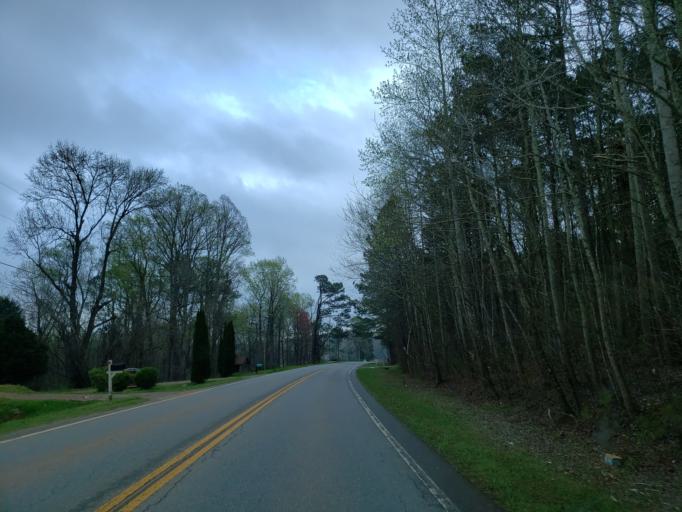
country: US
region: Georgia
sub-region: Polk County
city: Rockmart
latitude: 33.9240
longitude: -84.9839
